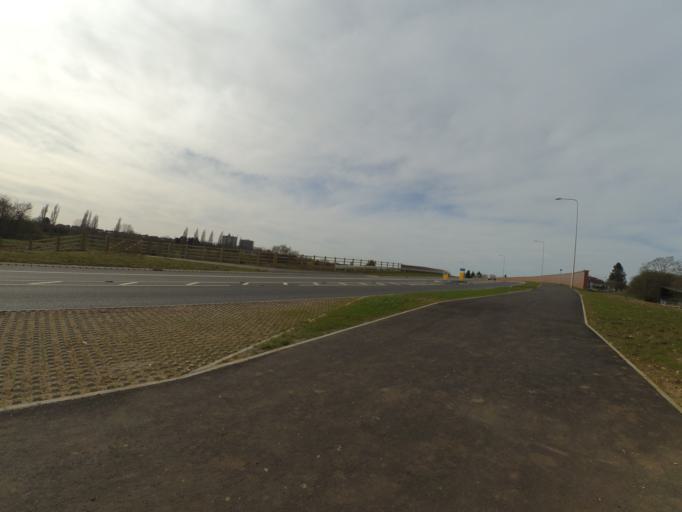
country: GB
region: England
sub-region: Warwickshire
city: Rugby
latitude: 52.3780
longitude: -1.2310
